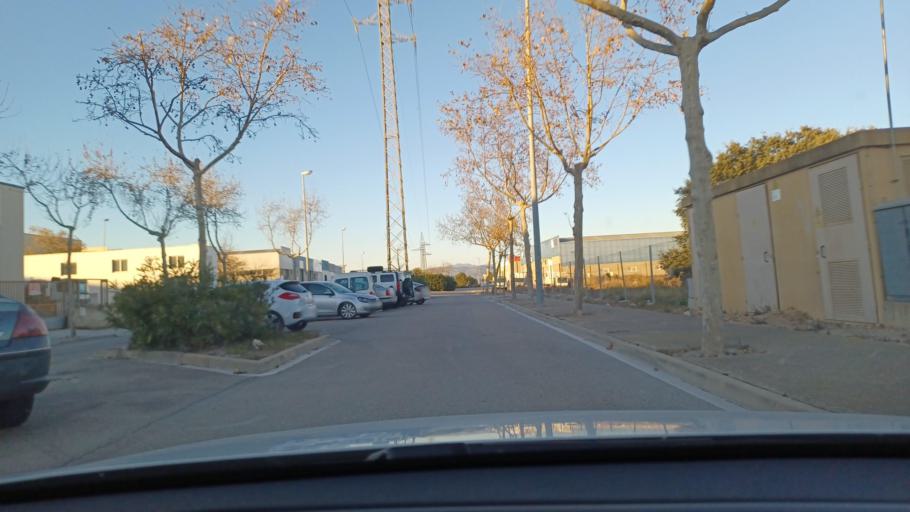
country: ES
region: Catalonia
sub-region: Provincia de Tarragona
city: Amposta
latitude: 40.7037
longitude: 0.5617
